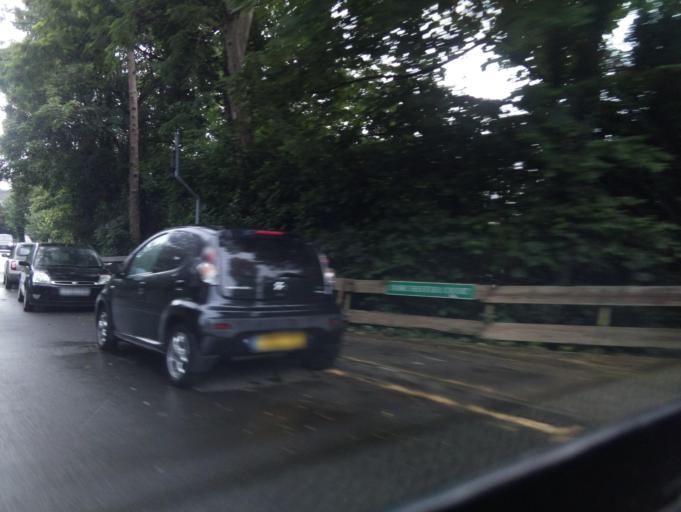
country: GB
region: England
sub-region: Surrey
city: Redhill
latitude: 51.2405
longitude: -0.1880
